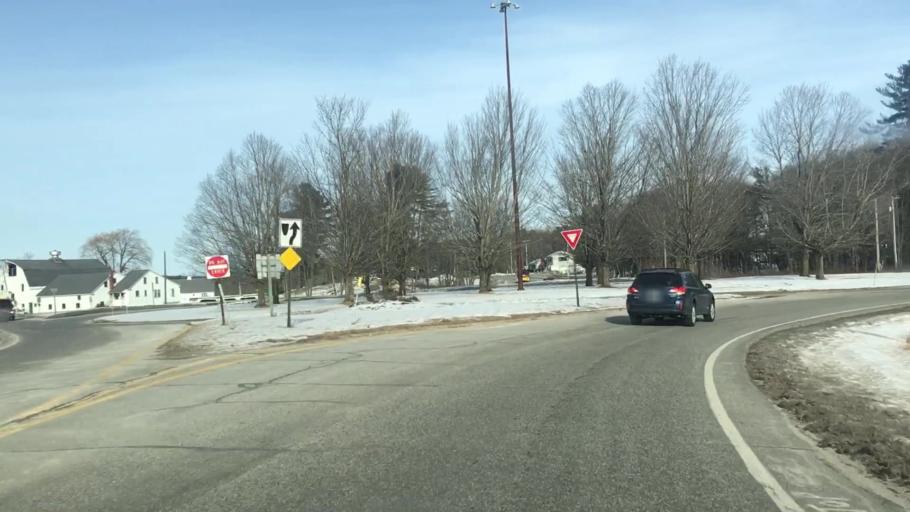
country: US
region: Maine
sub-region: Cumberland County
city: North Windham
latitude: 43.8021
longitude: -70.4065
